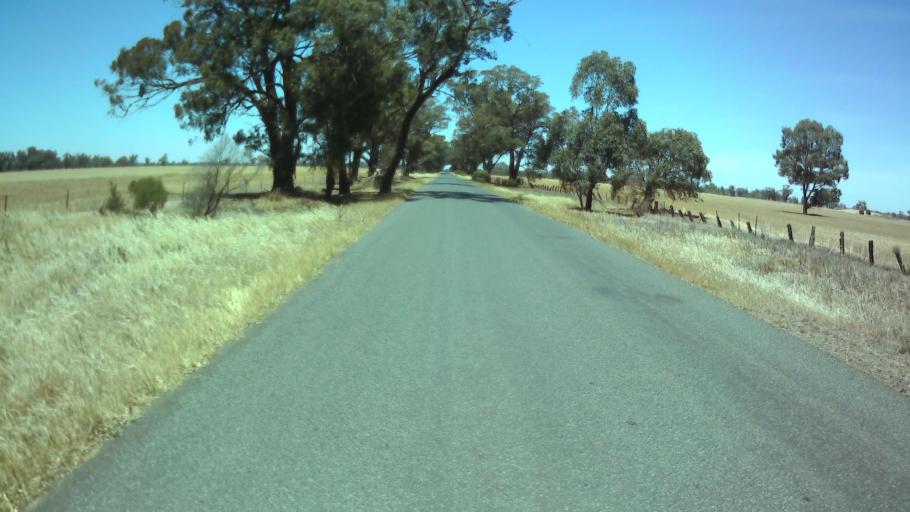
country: AU
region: New South Wales
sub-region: Weddin
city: Grenfell
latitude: -34.0185
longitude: 147.7931
